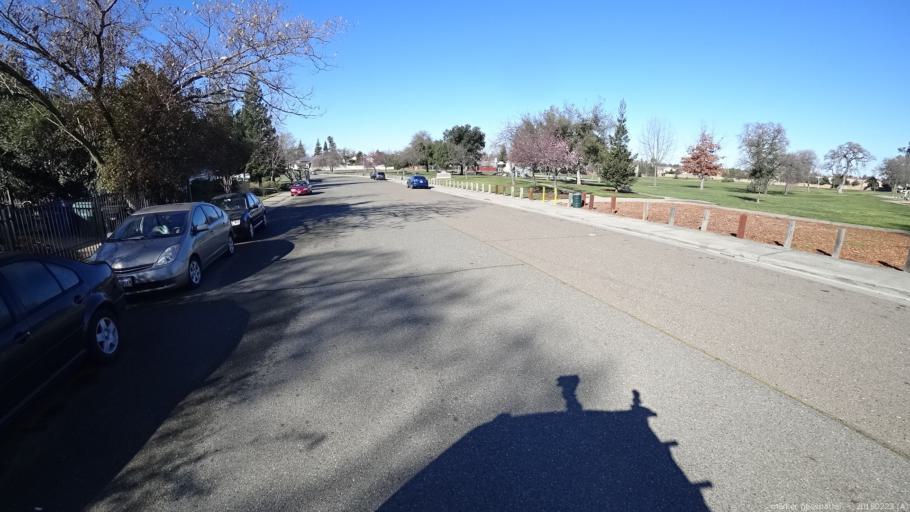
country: US
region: California
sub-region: Sacramento County
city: North Highlands
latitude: 38.7088
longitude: -121.3647
